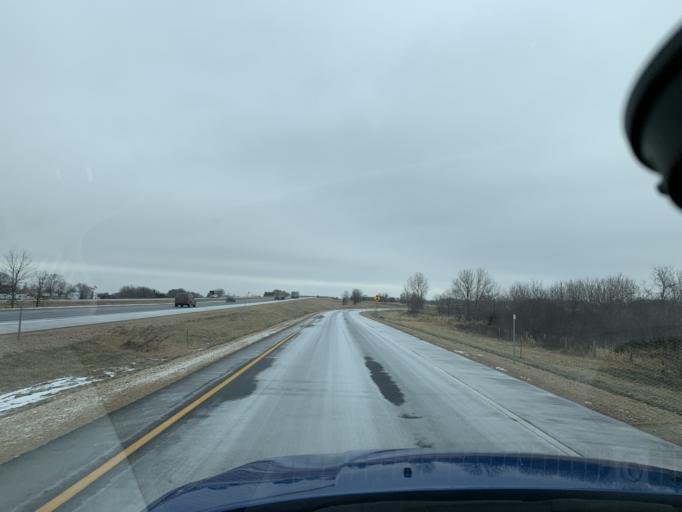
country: US
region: Wisconsin
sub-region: Dane County
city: Sun Prairie
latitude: 43.2366
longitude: -89.1499
